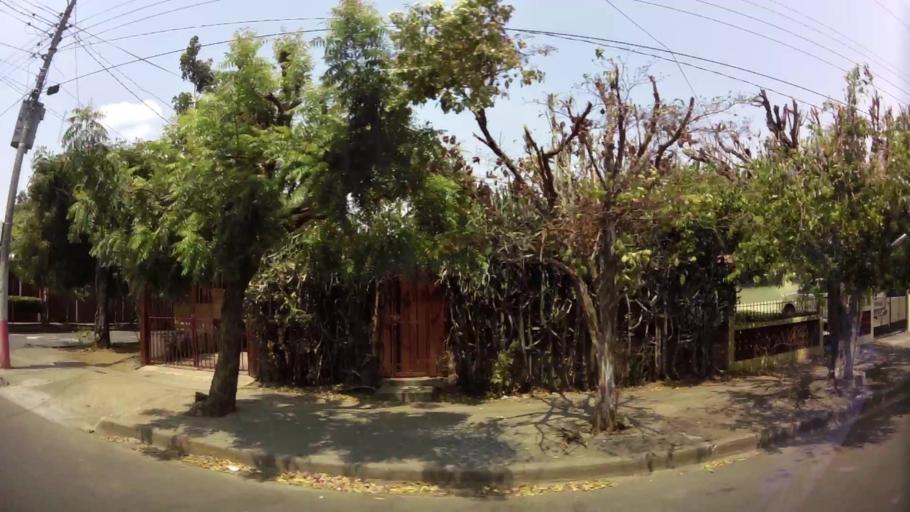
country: NI
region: Managua
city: Ciudad Sandino
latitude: 12.1530
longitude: -86.3142
